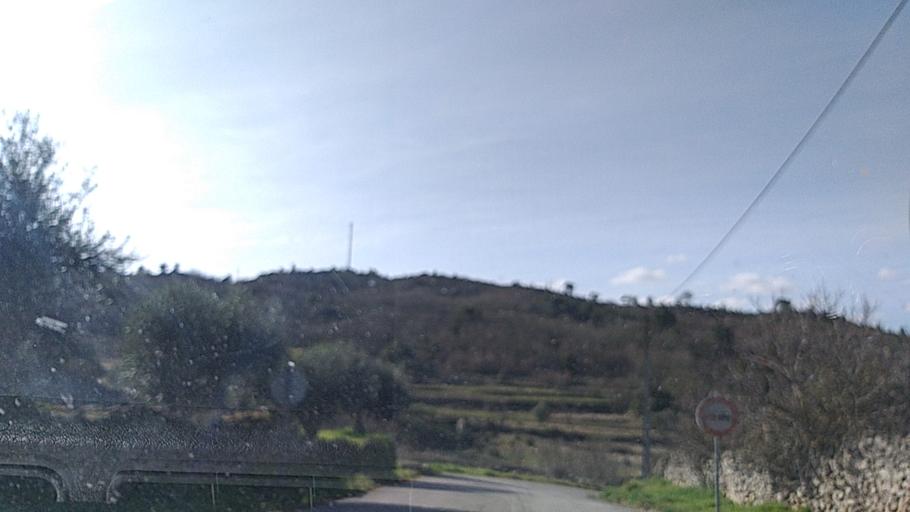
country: PT
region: Guarda
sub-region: Celorico da Beira
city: Celorico da Beira
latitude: 40.6397
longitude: -7.3956
